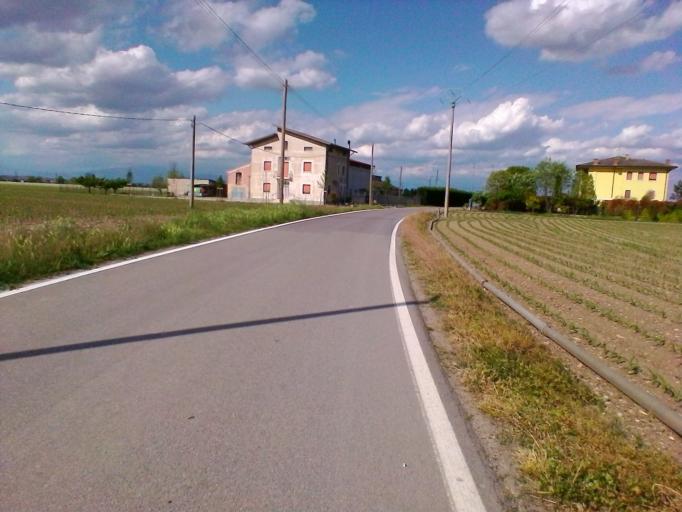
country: IT
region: Veneto
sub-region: Provincia di Verona
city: Mozzecane
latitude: 45.3011
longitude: 10.8415
